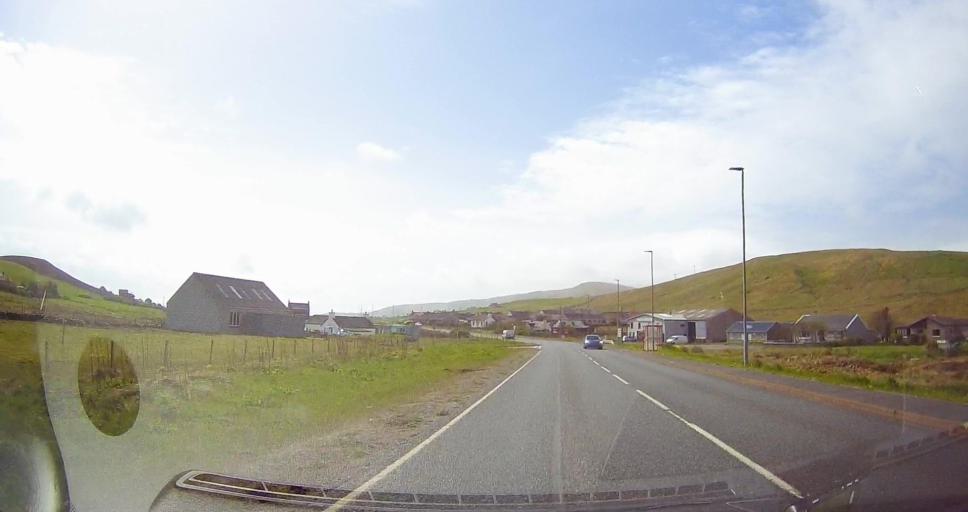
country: GB
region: Scotland
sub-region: Shetland Islands
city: Sandwick
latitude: 60.0570
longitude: -1.2246
